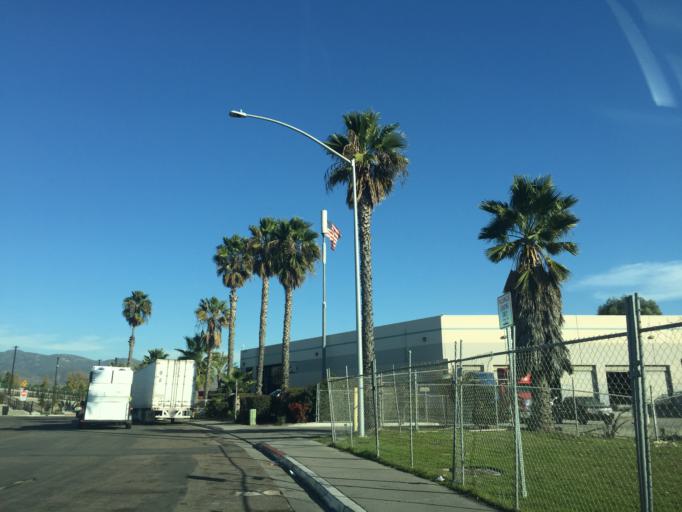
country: MX
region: Baja California
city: Tijuana
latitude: 32.5532
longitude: -116.9417
